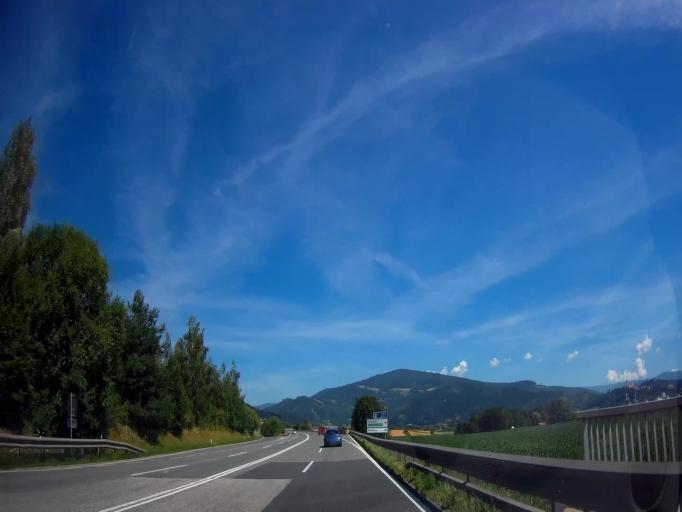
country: AT
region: Carinthia
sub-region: Politischer Bezirk Sankt Veit an der Glan
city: Molbling
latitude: 46.8599
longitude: 14.4496
